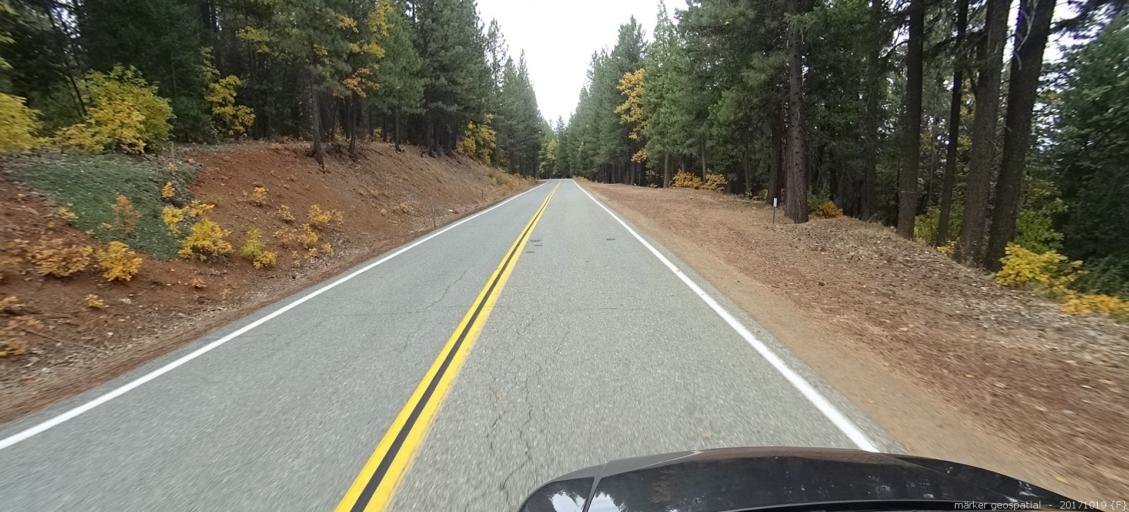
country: US
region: California
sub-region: Shasta County
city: Burney
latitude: 41.1246
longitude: -121.5906
